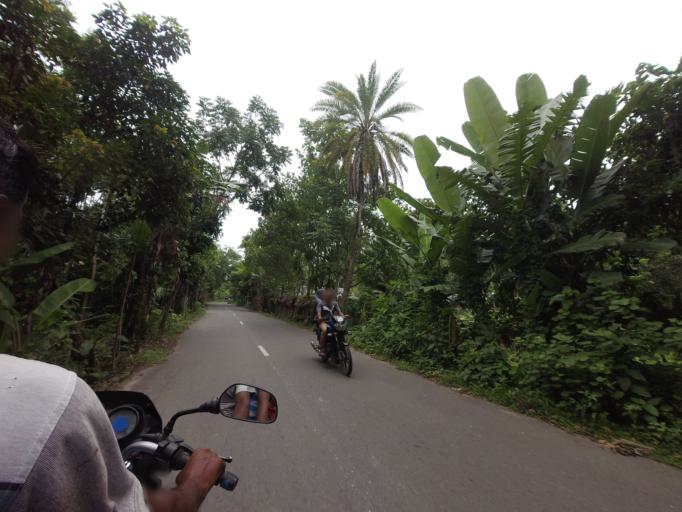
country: BD
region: Khulna
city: Kalia
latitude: 23.1597
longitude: 89.6440
